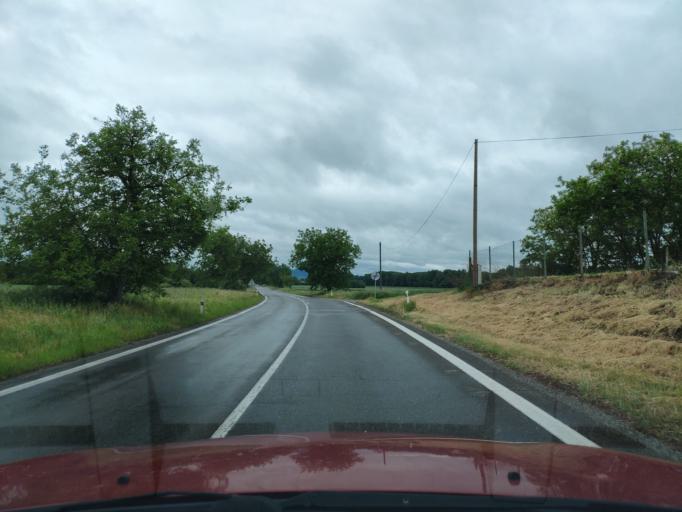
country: HU
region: Borsod-Abauj-Zemplen
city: Karcsa
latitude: 48.3918
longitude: 21.7696
